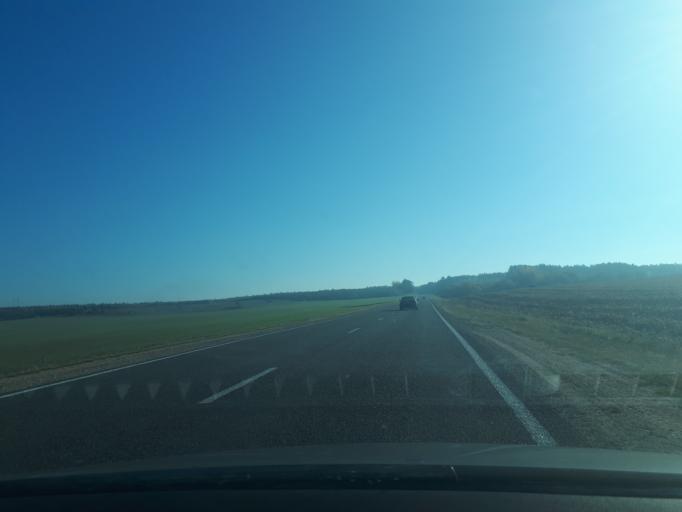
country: BY
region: Grodnenskaya
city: Zel'va
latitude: 53.1436
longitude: 24.8800
